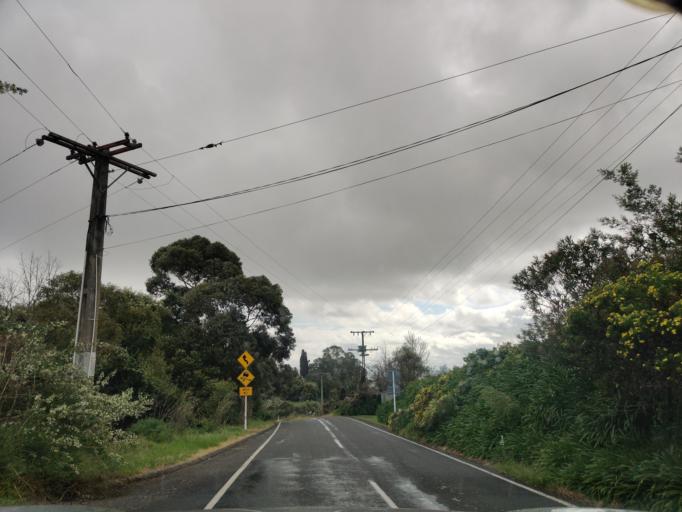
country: NZ
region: Hawke's Bay
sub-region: Hastings District
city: Hastings
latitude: -39.6809
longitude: 176.8971
